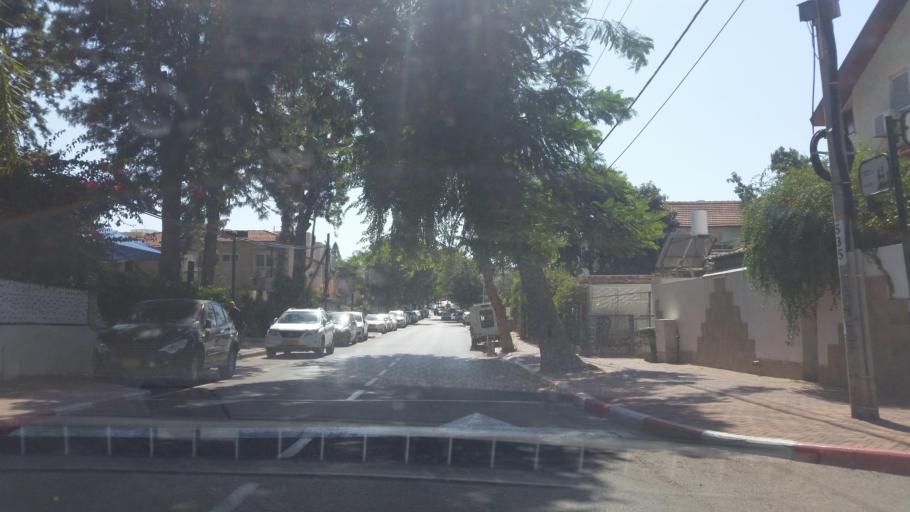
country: IL
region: Central District
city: Ra'anana
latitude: 32.1833
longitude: 34.8859
